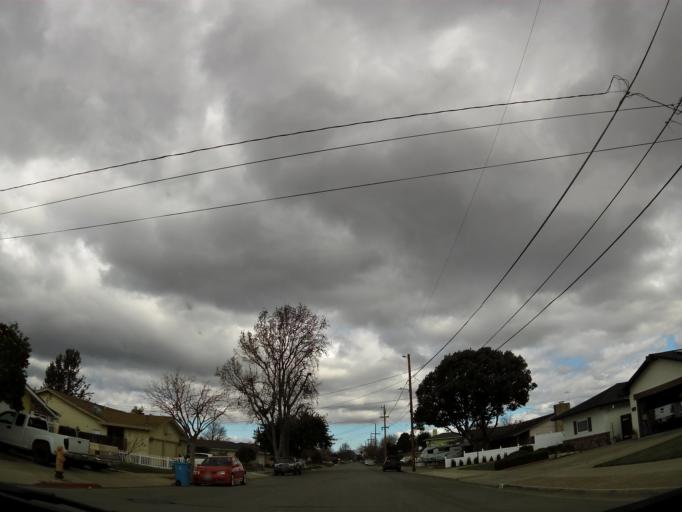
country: US
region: California
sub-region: San Benito County
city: Hollister
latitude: 36.8344
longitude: -121.3995
